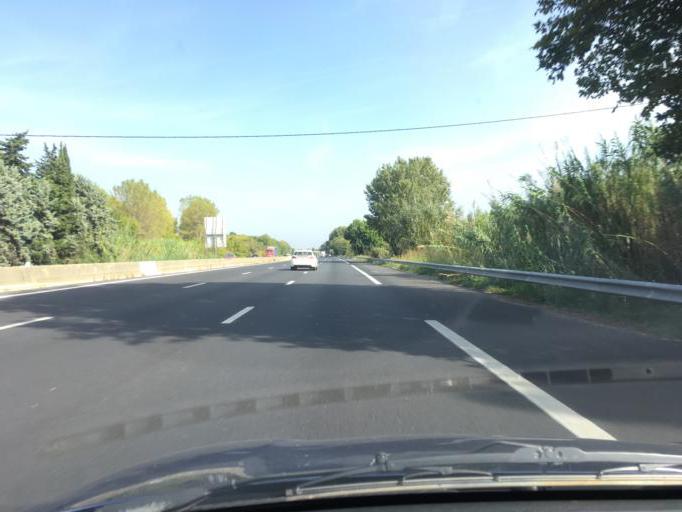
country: FR
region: Languedoc-Roussillon
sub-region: Departement du Gard
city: Caissargues
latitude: 43.8185
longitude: 4.3729
